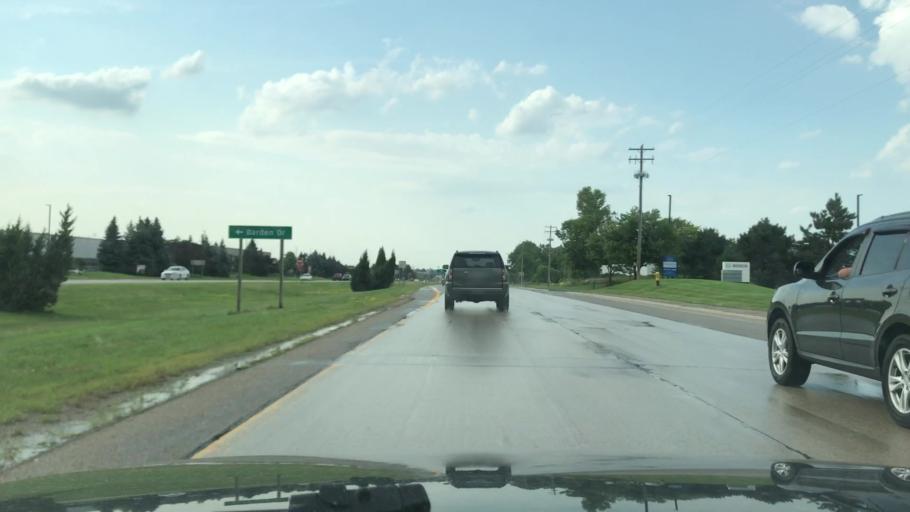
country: US
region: Michigan
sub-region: Kent County
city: East Grand Rapids
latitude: 42.8772
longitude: -85.5600
